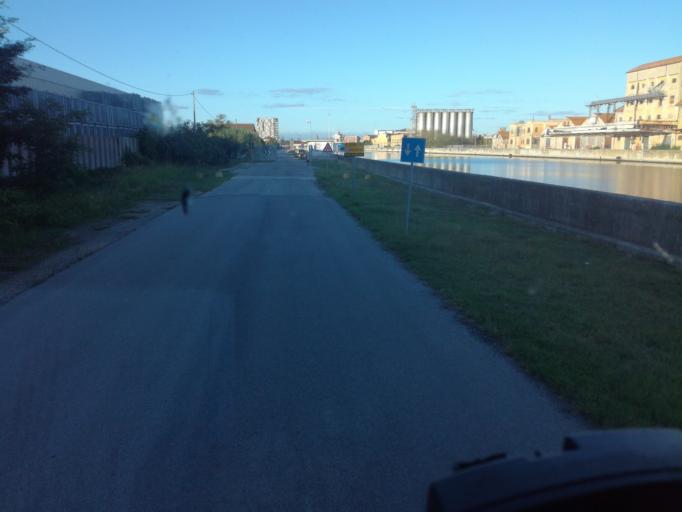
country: IT
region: Emilia-Romagna
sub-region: Provincia di Ravenna
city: Ravenna
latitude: 44.4274
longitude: 12.2233
